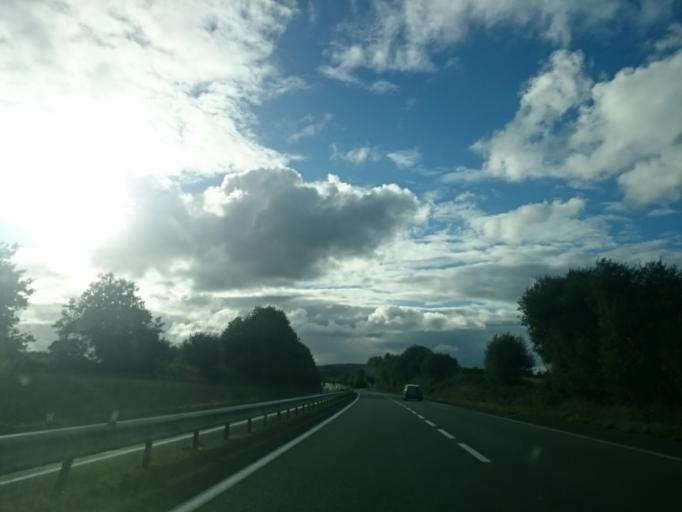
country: FR
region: Brittany
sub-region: Departement des Cotes-d'Armor
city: Pedernec
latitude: 48.5707
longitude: -3.2530
